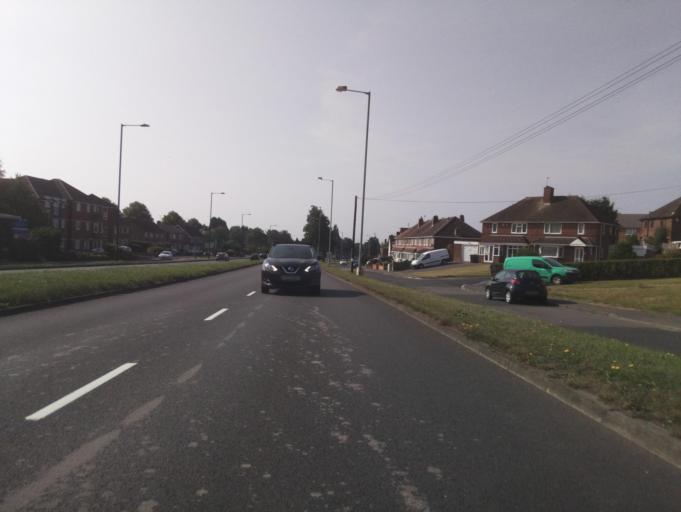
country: GB
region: England
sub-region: Walsall
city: Streetly
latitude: 52.5581
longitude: -1.8974
